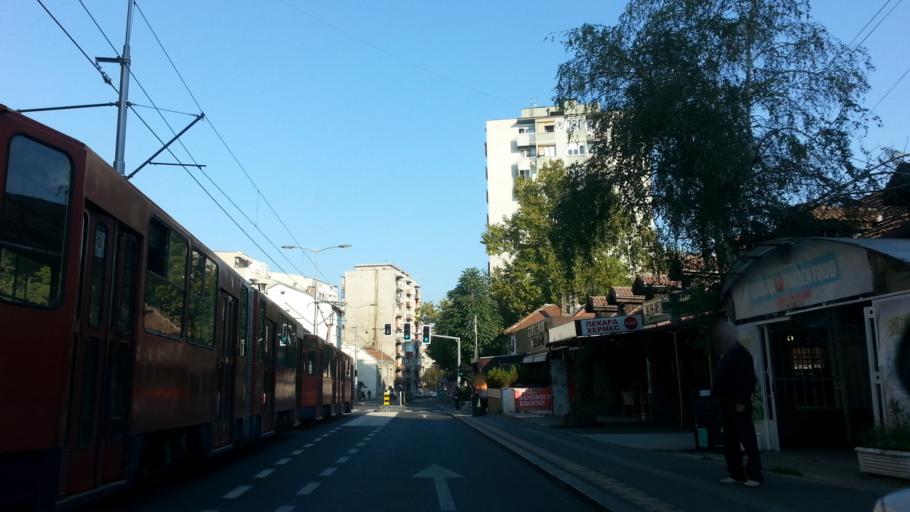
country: RS
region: Central Serbia
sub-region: Belgrade
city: Vozdovac
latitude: 44.7684
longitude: 20.4798
